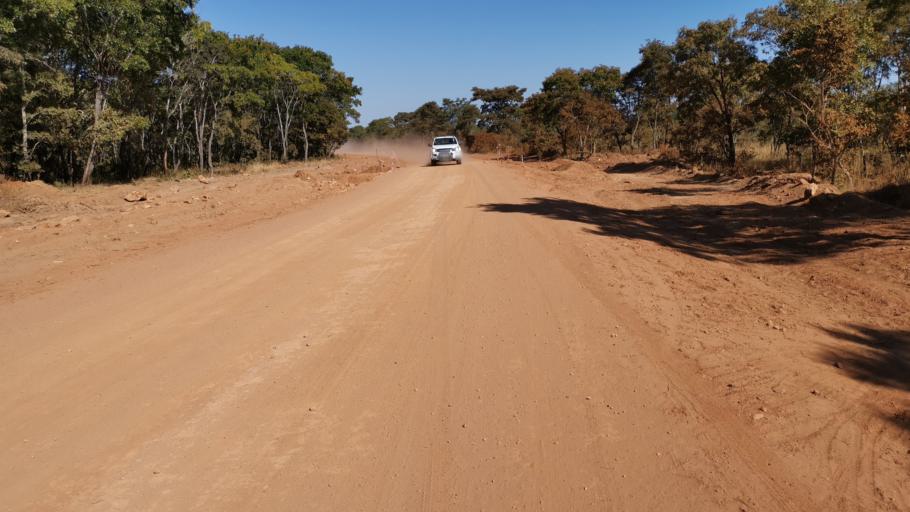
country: ZM
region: Central
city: Mkushi
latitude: -13.9924
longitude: 29.4903
